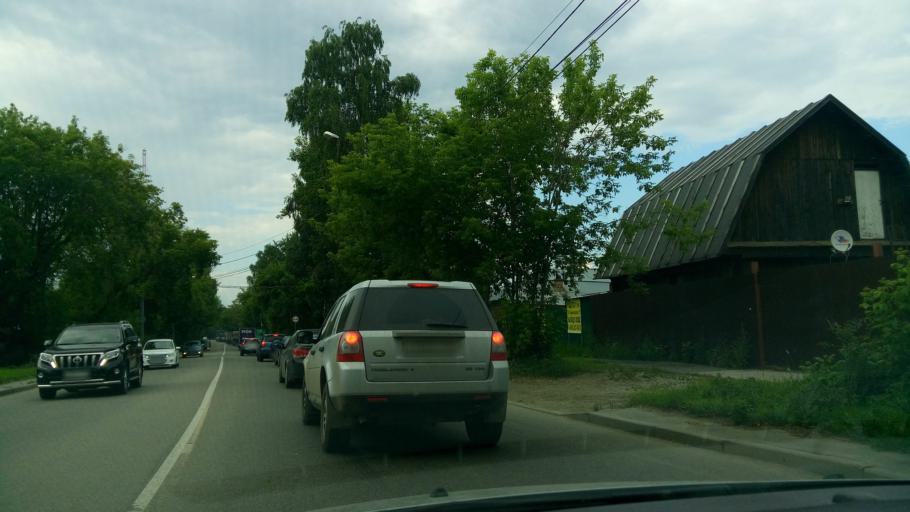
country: RU
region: Sverdlovsk
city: Yekaterinburg
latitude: 56.8781
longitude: 60.6924
